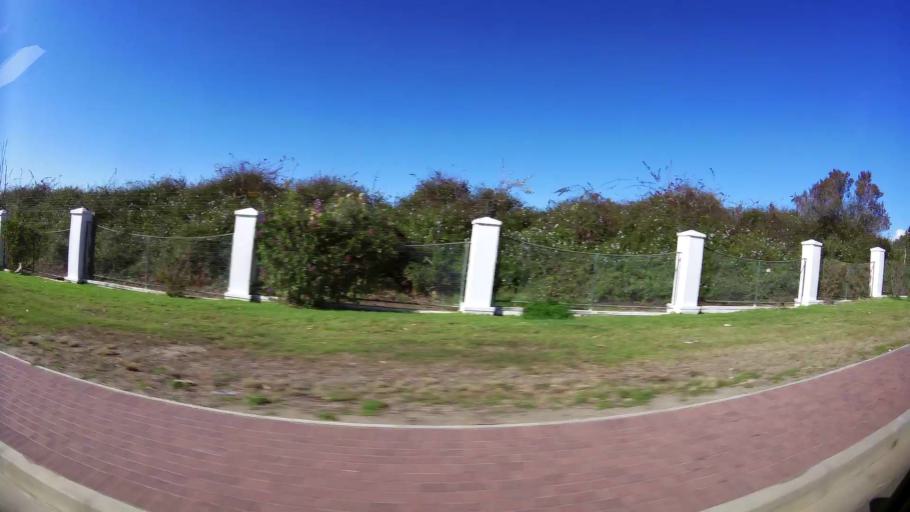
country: ZA
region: Western Cape
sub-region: Eden District Municipality
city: George
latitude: -33.9533
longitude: 22.4008
